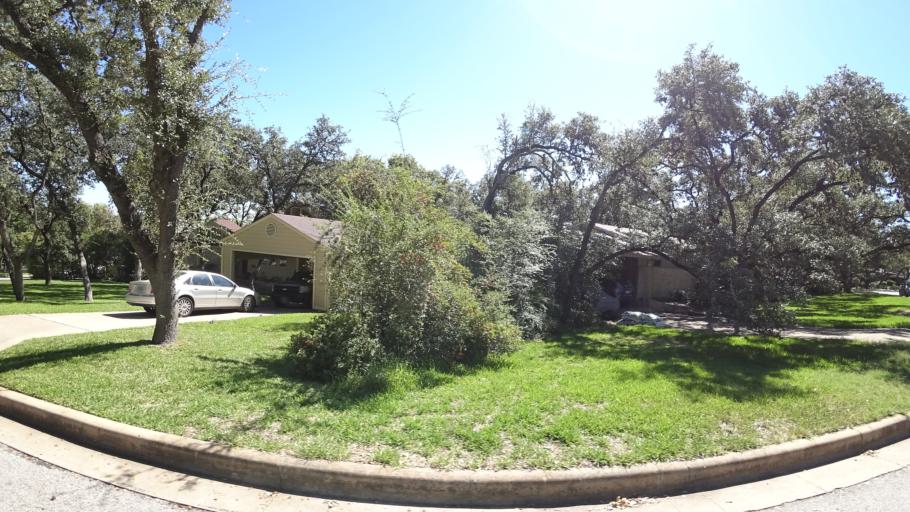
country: US
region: Texas
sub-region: Travis County
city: West Lake Hills
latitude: 30.3342
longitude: -97.7609
